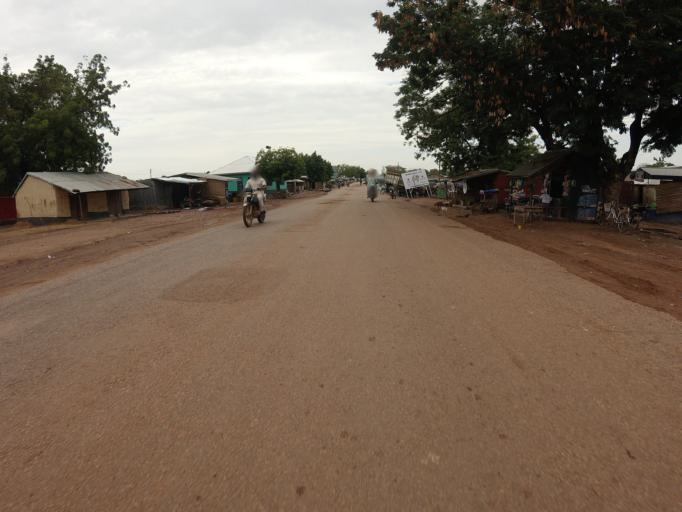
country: GH
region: Upper East
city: Bawku
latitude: 10.9379
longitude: -0.4883
